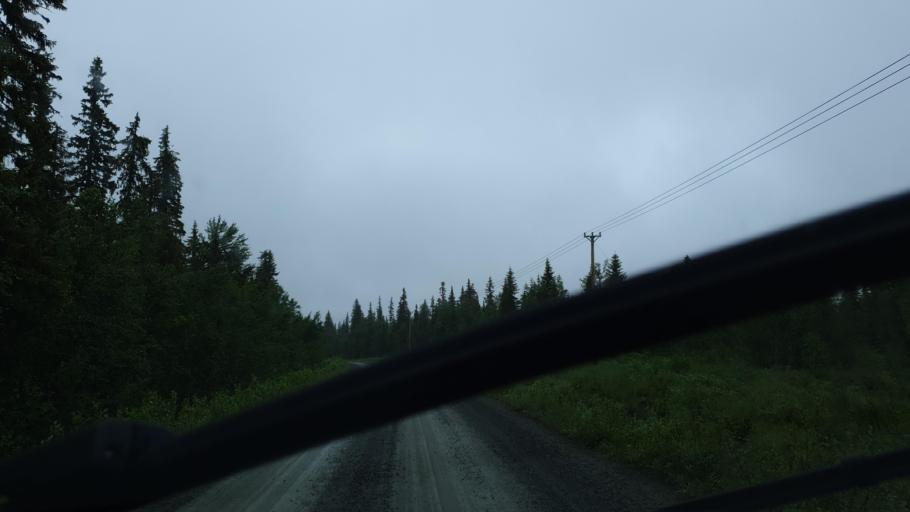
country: SE
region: Vaesterbotten
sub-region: Vilhelmina Kommun
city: Sjoberg
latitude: 65.3113
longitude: 15.9701
